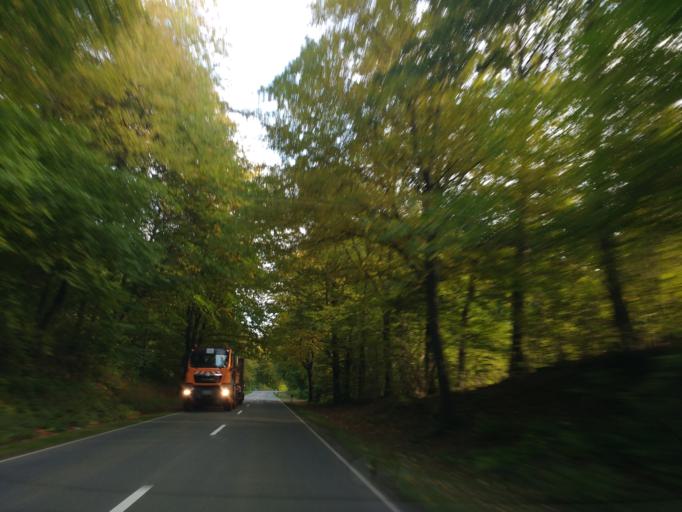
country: DE
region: Schleswig-Holstein
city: Schonwalde am Bungsberg
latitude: 54.2075
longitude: 10.7421
